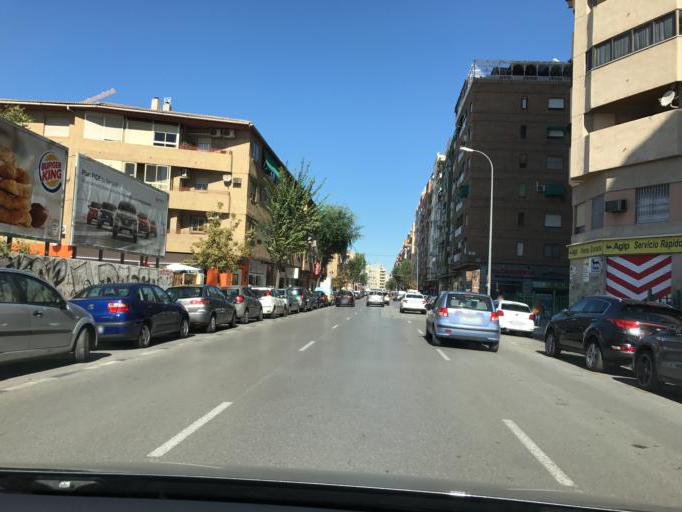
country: ES
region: Andalusia
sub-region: Provincia de Granada
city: Granada
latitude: 37.1746
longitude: -3.6101
